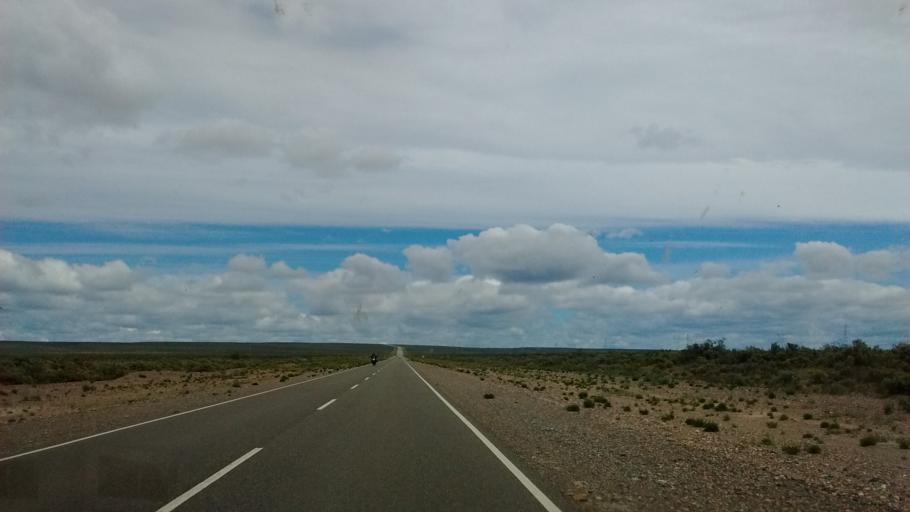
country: AR
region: Neuquen
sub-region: Departamento de Picun Leufu
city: Picun Leufu
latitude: -39.7153
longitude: -69.5256
